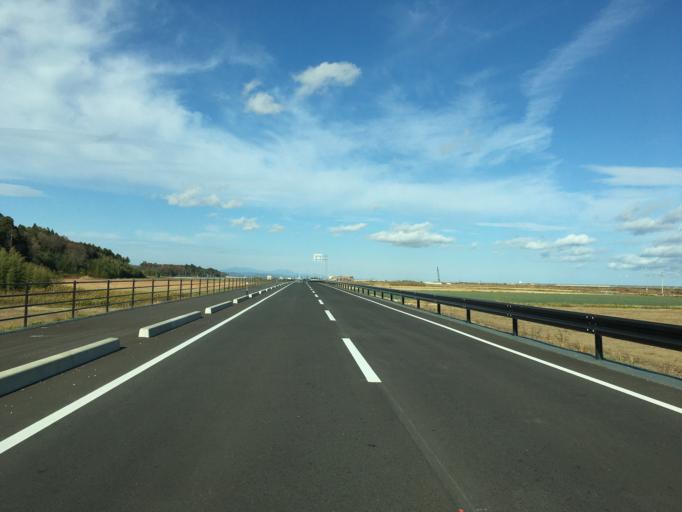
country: JP
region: Miyagi
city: Watari
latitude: 37.9033
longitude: 140.9218
